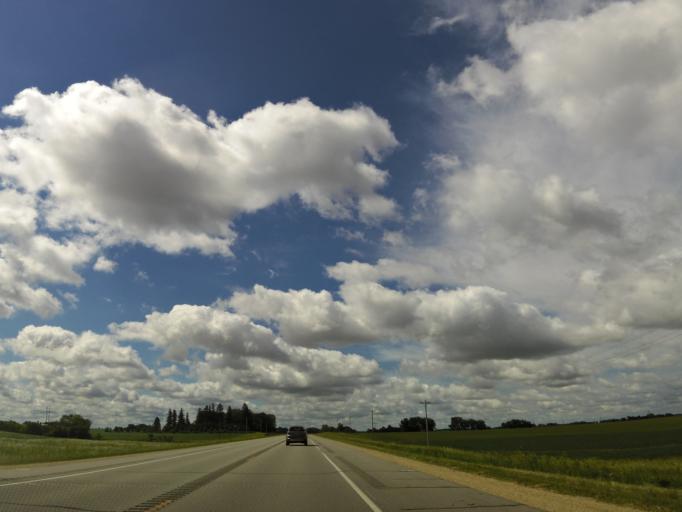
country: US
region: Minnesota
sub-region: Olmsted County
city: Stewartville
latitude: 43.8323
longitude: -92.4893
